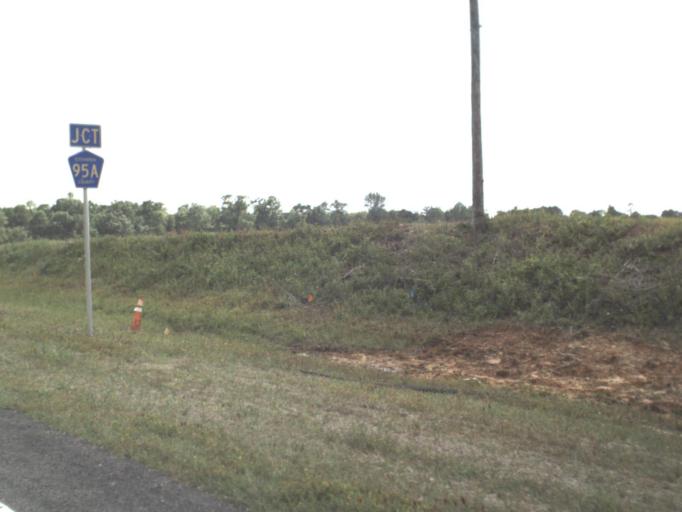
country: US
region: Florida
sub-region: Escambia County
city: Molino
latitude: 30.7420
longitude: -87.3486
